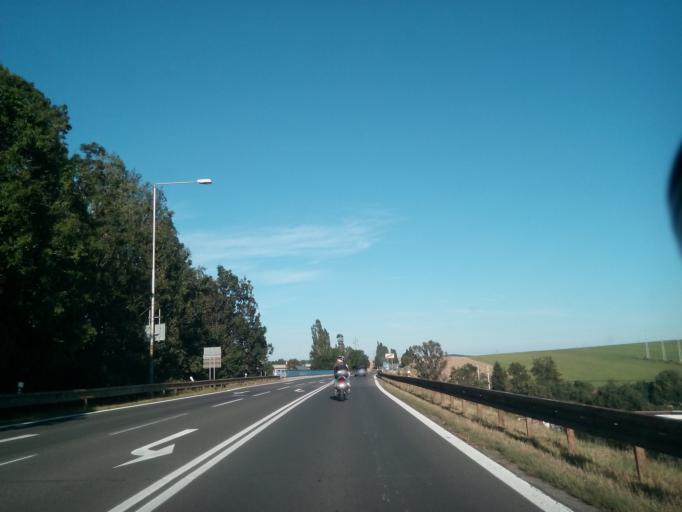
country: SK
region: Presovsky
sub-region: Okres Poprad
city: Poprad
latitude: 49.0498
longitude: 20.3067
